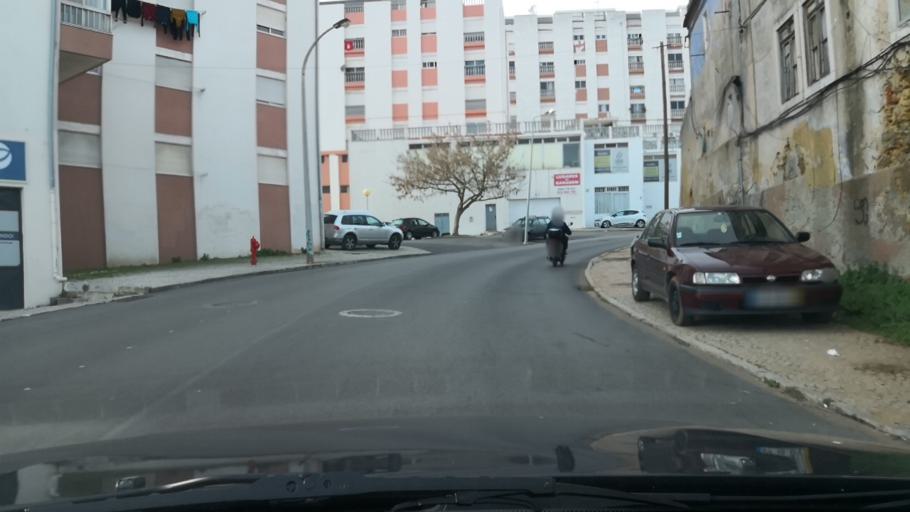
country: PT
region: Setubal
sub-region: Setubal
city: Setubal
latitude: 38.5228
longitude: -8.9040
